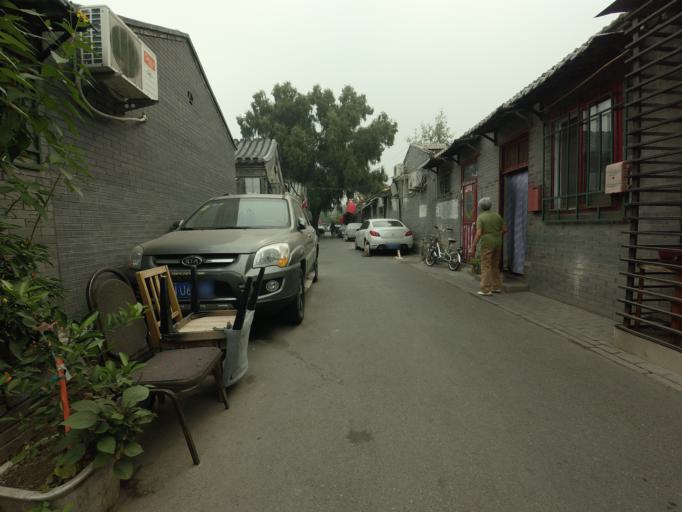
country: CN
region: Beijing
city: Jingshan
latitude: 39.9379
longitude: 116.3761
